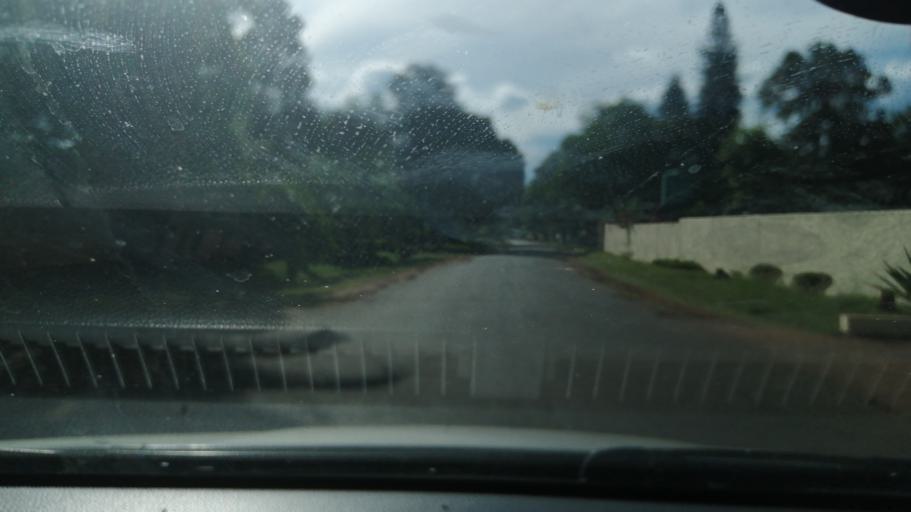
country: ZW
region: Harare
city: Harare
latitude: -17.7649
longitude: 31.0556
